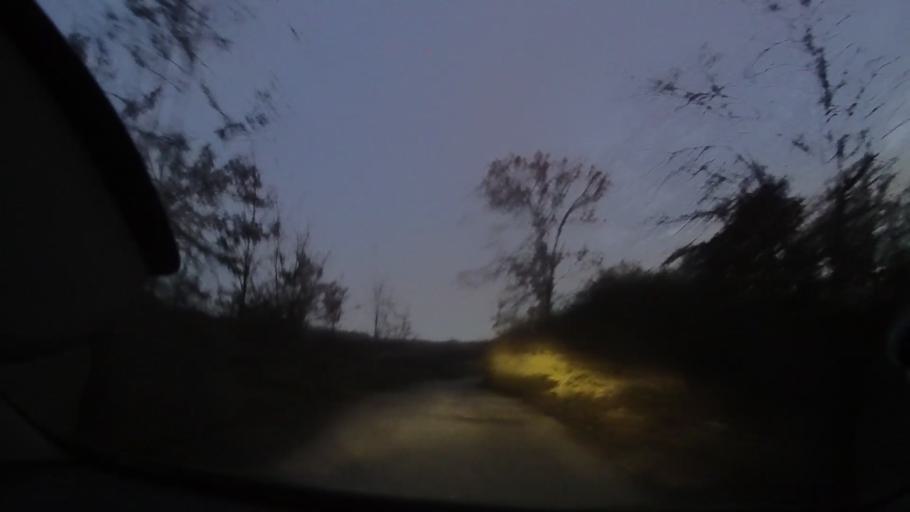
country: RO
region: Bihor
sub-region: Comuna Tetchea
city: Hotar
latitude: 47.0033
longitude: 22.3094
